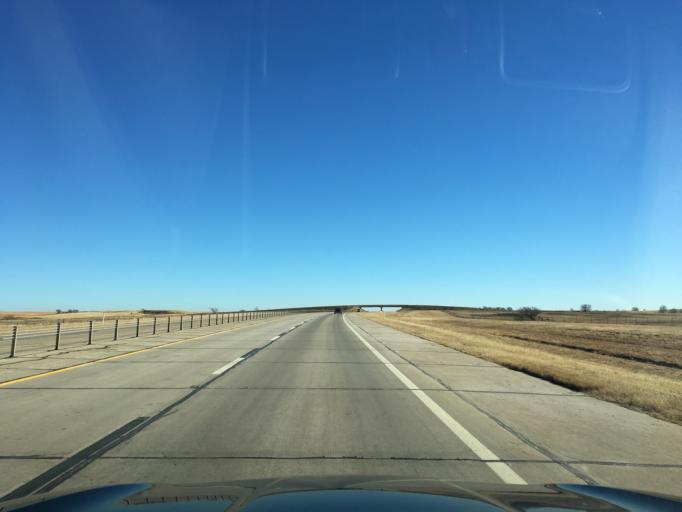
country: US
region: Oklahoma
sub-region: Noble County
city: Perry
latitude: 36.4025
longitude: -97.2543
